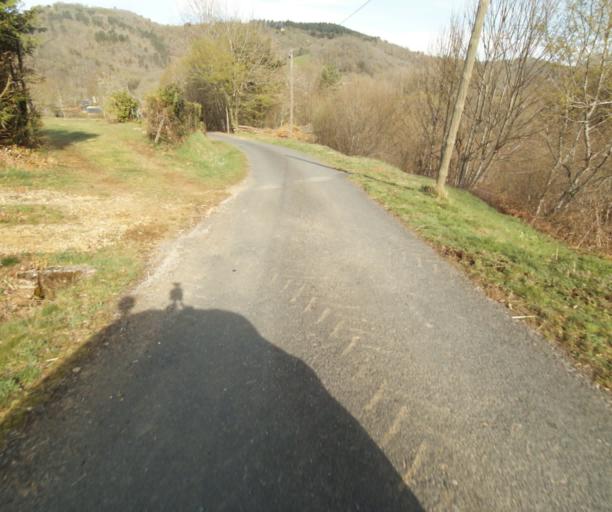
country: FR
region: Limousin
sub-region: Departement de la Correze
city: Naves
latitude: 45.3289
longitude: 1.8182
